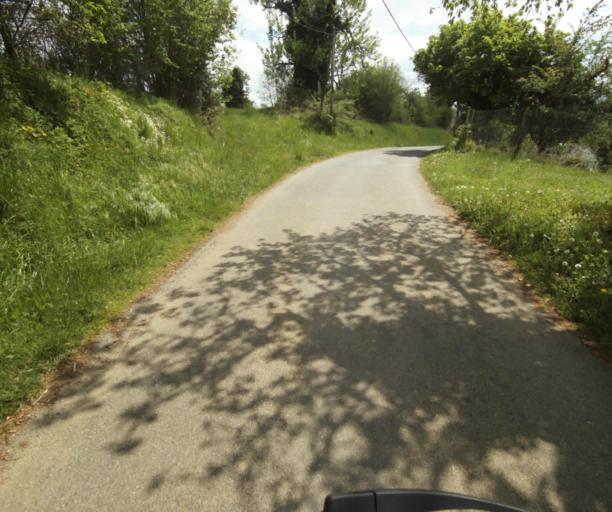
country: FR
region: Limousin
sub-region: Departement de la Correze
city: Tulle
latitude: 45.2810
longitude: 1.7601
